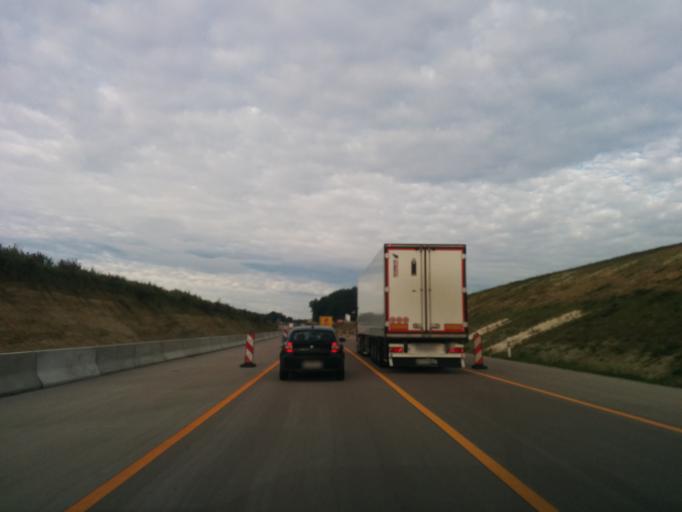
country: DE
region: Bavaria
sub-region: Swabia
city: Zusmarshausen
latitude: 48.4089
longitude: 10.5826
